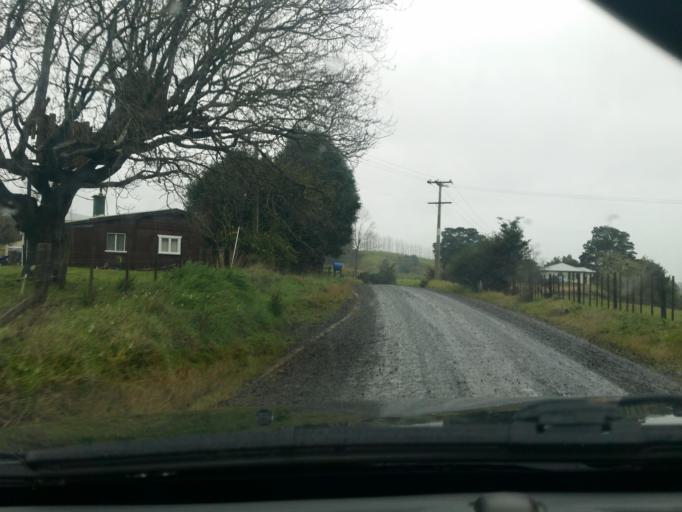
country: NZ
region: Northland
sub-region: Kaipara District
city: Dargaville
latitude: -35.7677
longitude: 173.7016
